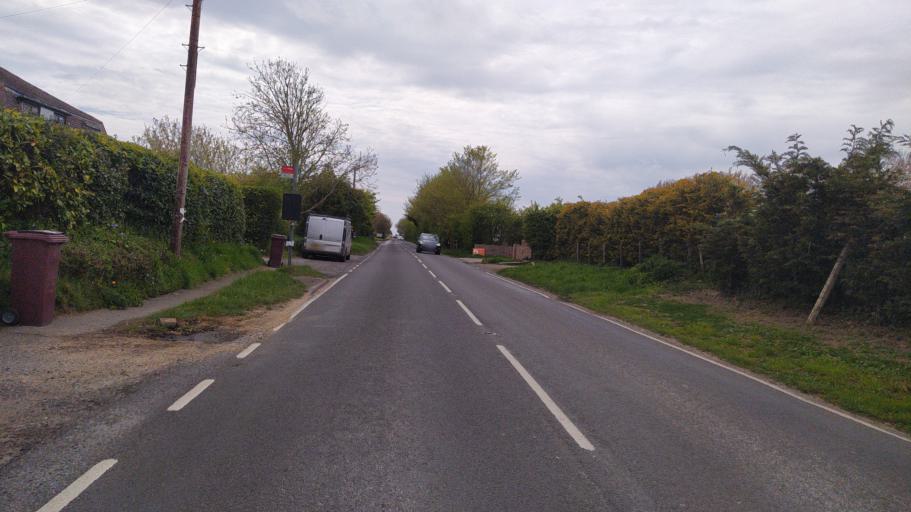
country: GB
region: England
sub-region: West Sussex
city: East Wittering
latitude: 50.7717
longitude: -0.8524
